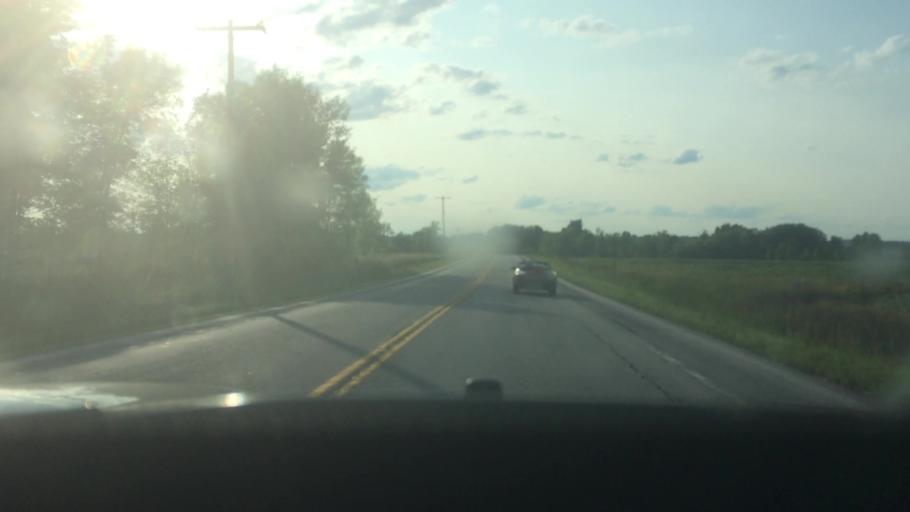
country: US
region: New York
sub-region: St. Lawrence County
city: Ogdensburg
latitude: 44.6595
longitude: -75.3306
